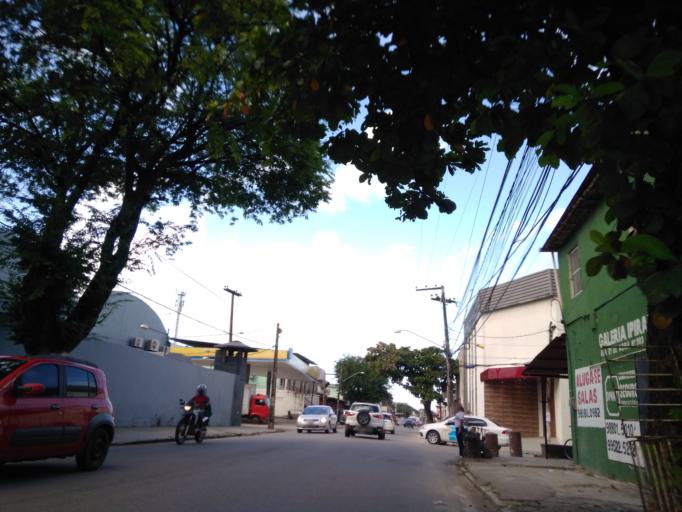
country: BR
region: Pernambuco
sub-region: Recife
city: Recife
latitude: -8.0757
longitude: -34.9160
